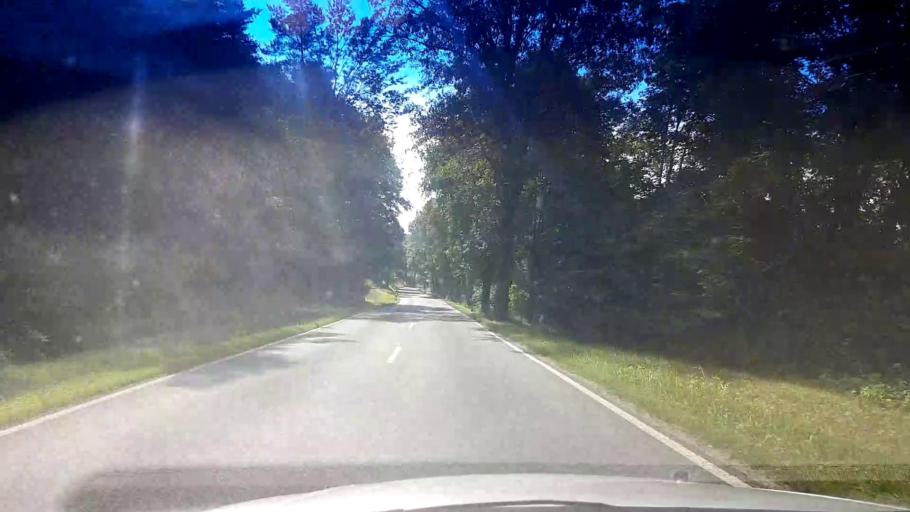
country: DE
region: Bavaria
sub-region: Upper Franconia
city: Hollfeld
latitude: 49.9394
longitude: 11.3405
